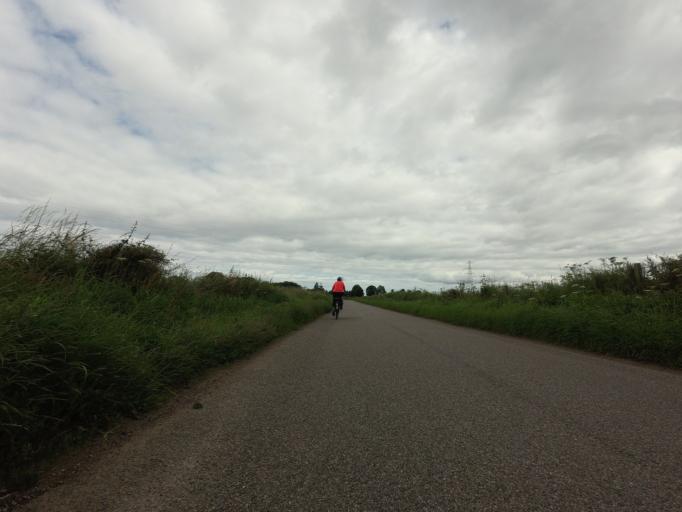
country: GB
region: Scotland
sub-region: Moray
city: Forres
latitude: 57.6144
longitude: -3.6546
